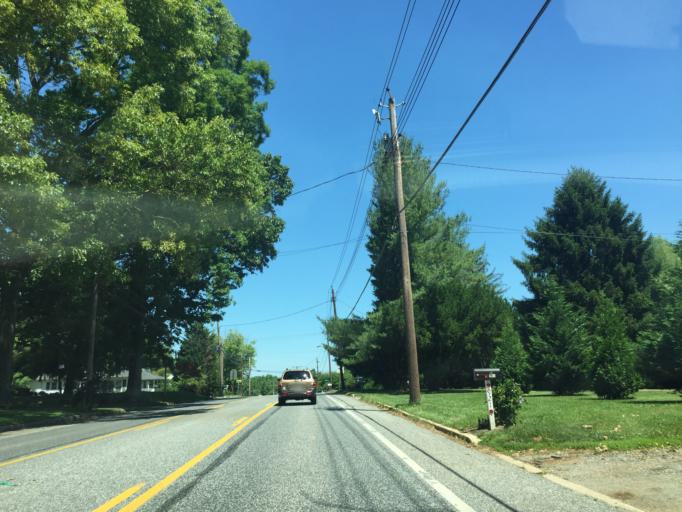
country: US
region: Maryland
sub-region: Harford County
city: Bel Air North
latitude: 39.5500
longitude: -76.3632
